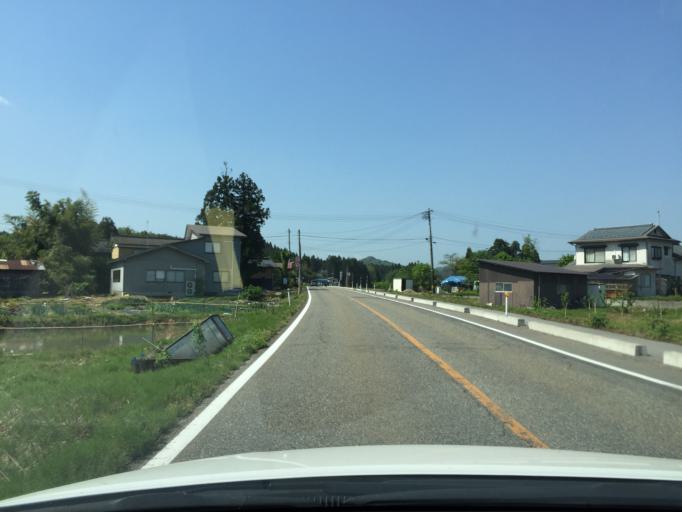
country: JP
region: Niigata
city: Muramatsu
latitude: 37.6717
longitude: 139.1473
